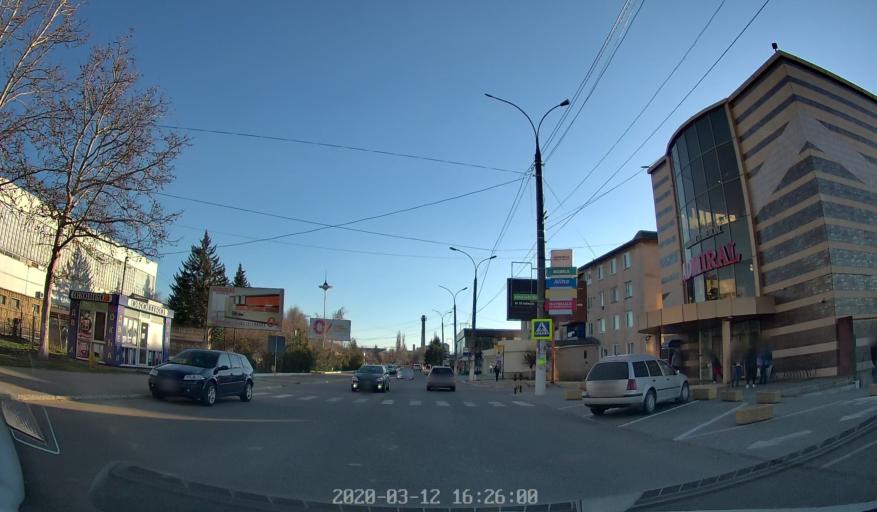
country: MD
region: Anenii Noi
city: Anenii Noi
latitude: 46.8827
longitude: 29.2331
